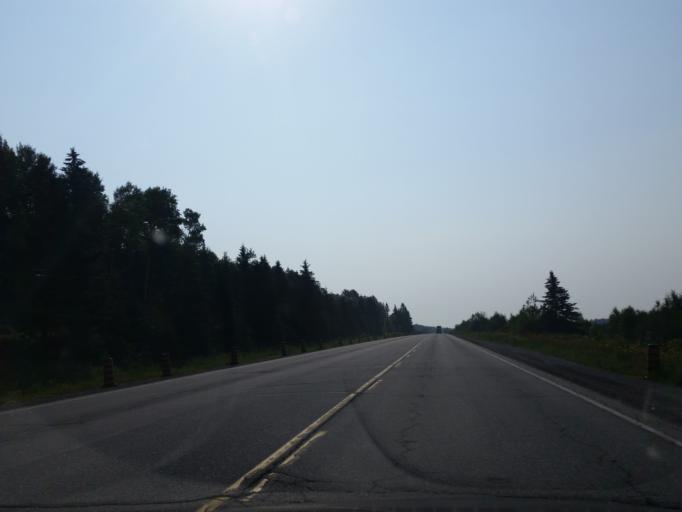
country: CA
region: Ontario
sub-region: Nipissing District
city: North Bay
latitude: 46.4273
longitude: -80.2027
